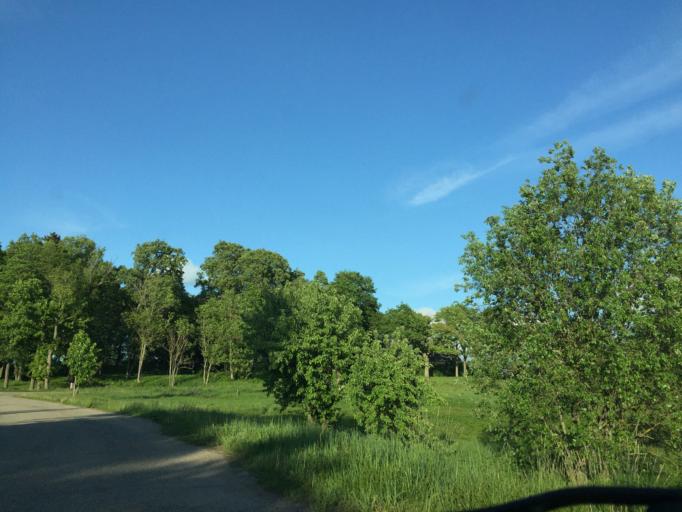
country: LV
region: Koceni
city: Koceni
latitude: 57.4669
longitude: 25.2624
